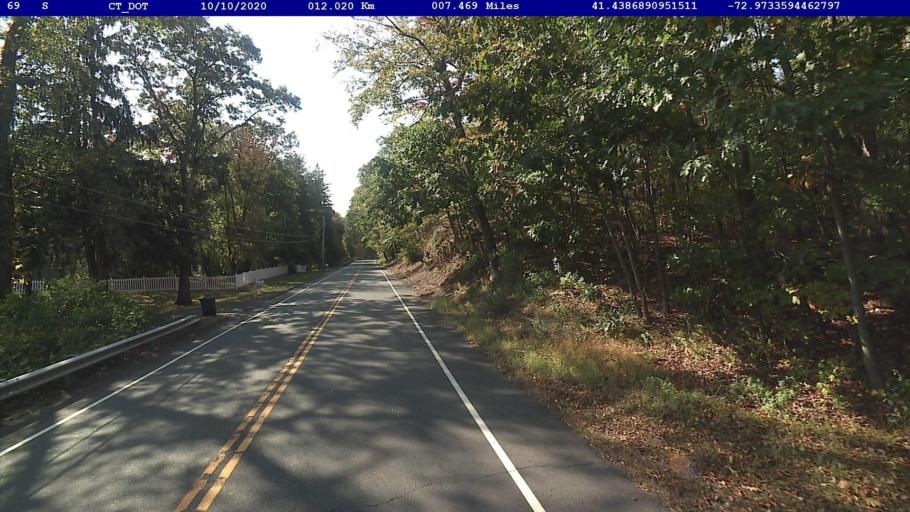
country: US
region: Connecticut
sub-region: New Haven County
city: Prospect
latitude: 41.4387
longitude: -72.9734
